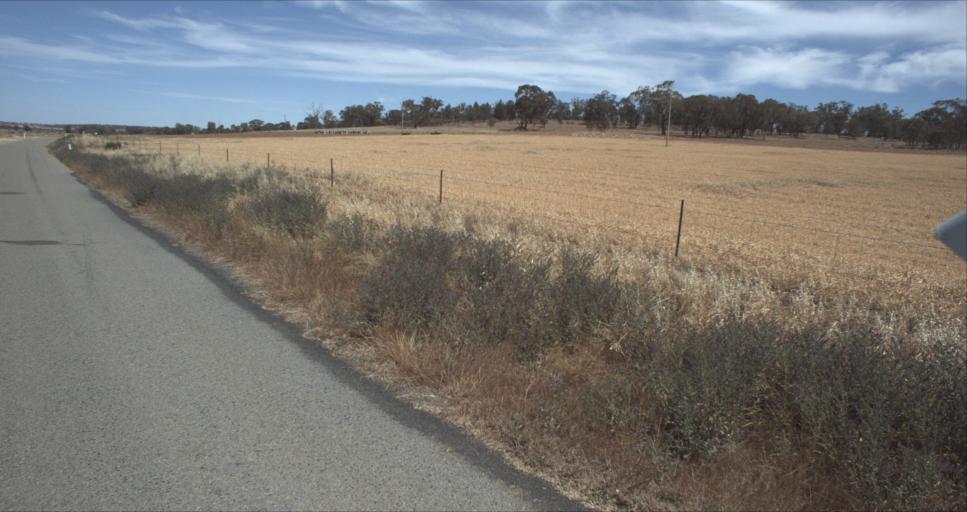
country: AU
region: New South Wales
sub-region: Leeton
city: Leeton
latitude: -34.5961
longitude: 146.4769
